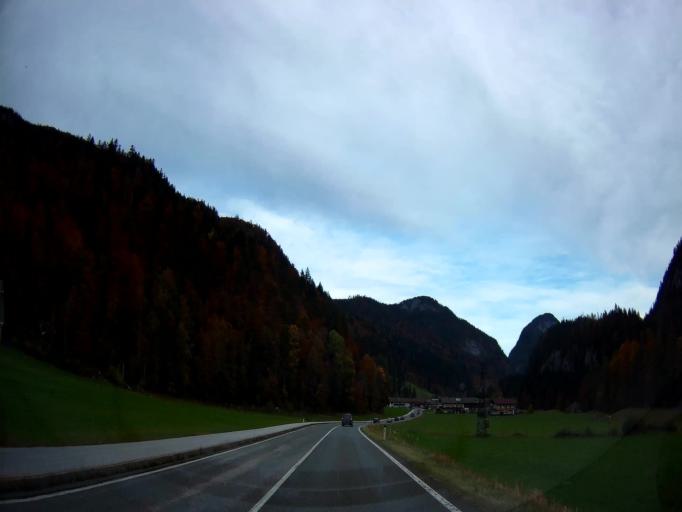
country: AT
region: Salzburg
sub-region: Politischer Bezirk Zell am See
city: Lofer
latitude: 47.6109
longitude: 12.7031
